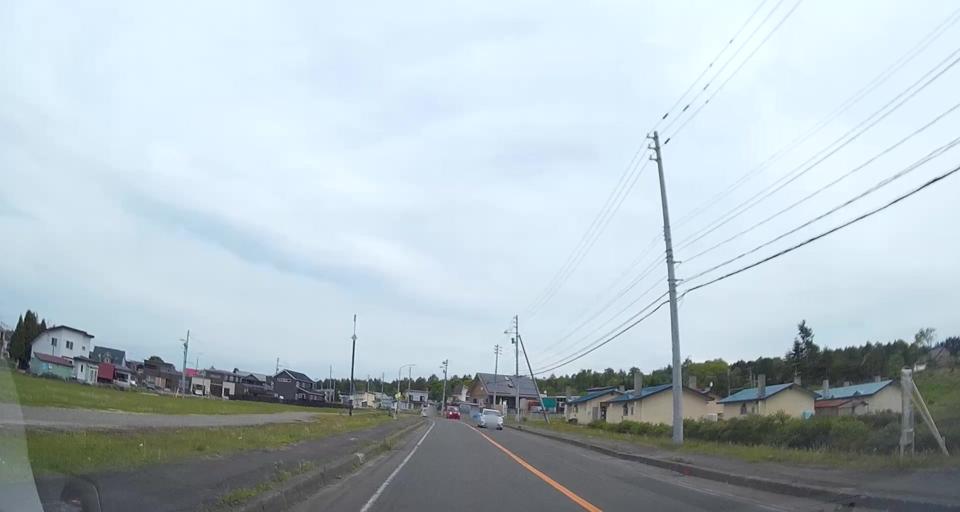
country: JP
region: Hokkaido
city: Chitose
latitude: 42.7706
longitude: 141.8284
